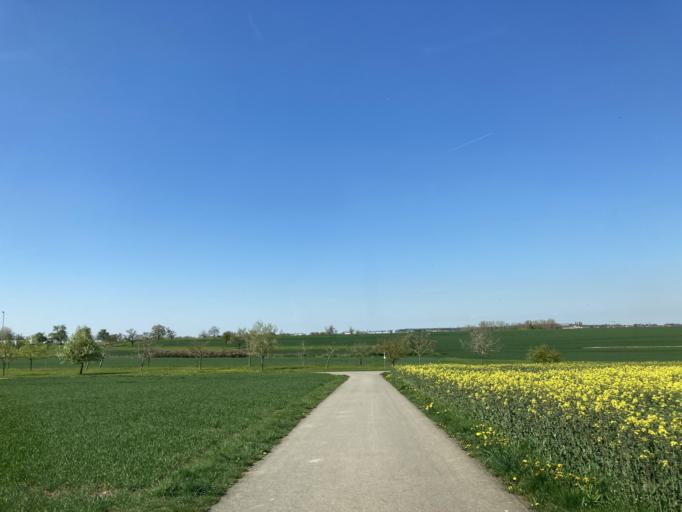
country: DE
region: Baden-Wuerttemberg
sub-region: Regierungsbezirk Stuttgart
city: Motzingen
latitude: 48.5138
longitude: 8.7581
